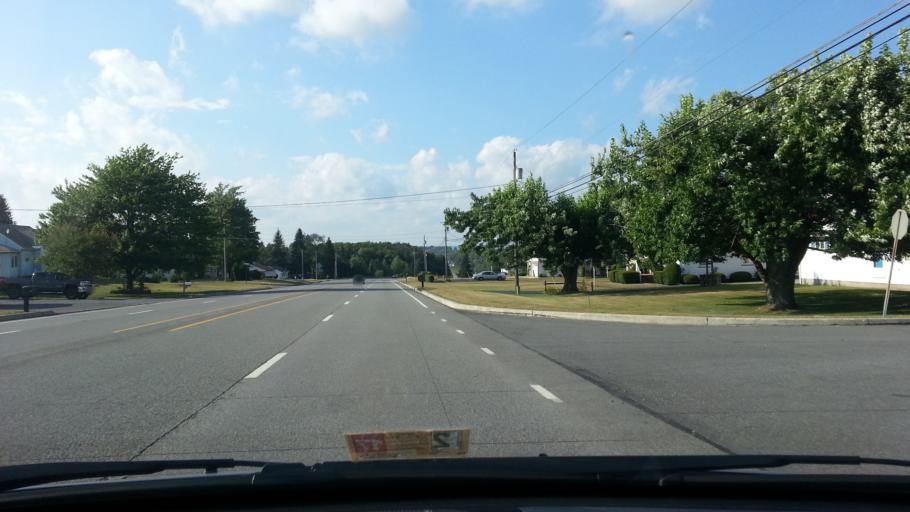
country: US
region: Pennsylvania
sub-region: Elk County
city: Saint Marys
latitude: 41.3761
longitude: -78.5585
